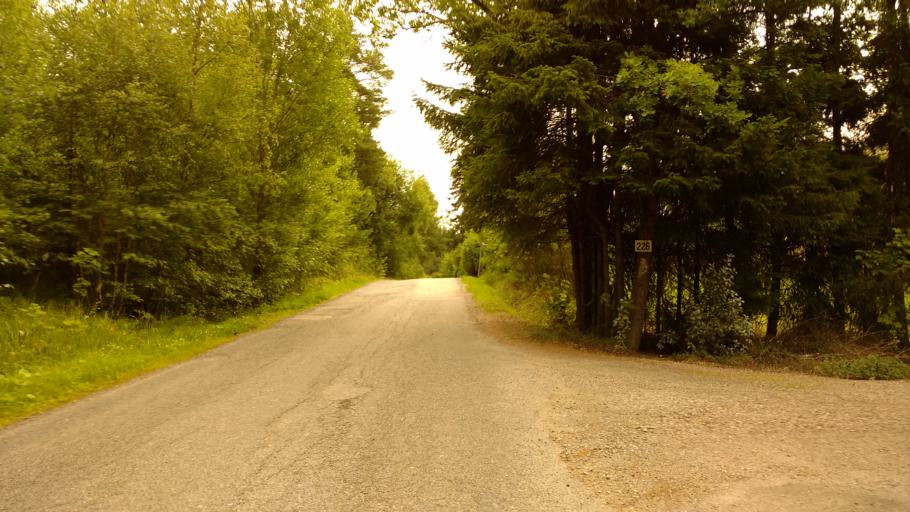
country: FI
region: Varsinais-Suomi
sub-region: Turku
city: Piikkioe
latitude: 60.4360
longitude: 22.4470
